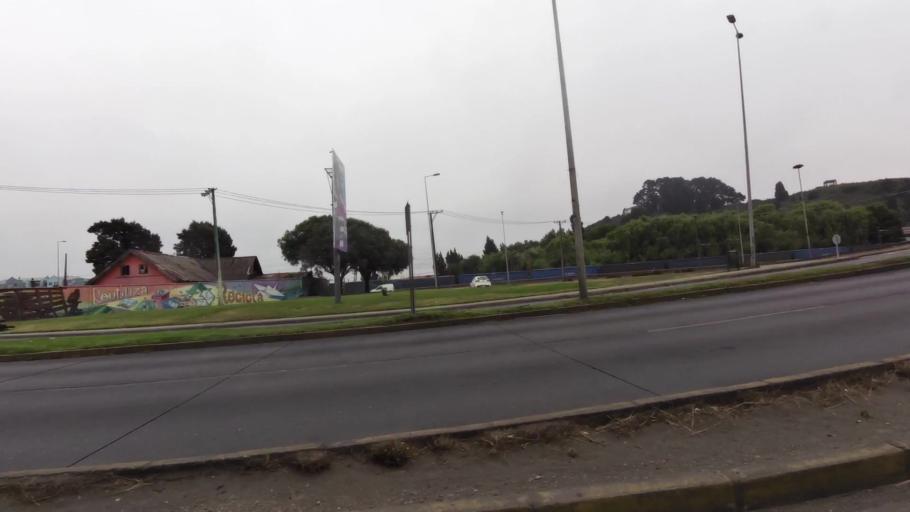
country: CL
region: Biobio
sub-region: Provincia de Concepcion
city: Concepcion
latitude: -36.8220
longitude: -73.0639
